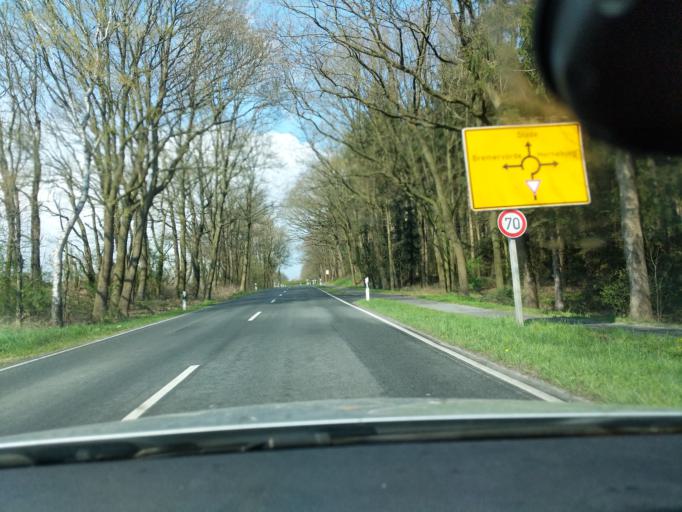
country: DE
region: Lower Saxony
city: Harsefeld
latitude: 53.4723
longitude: 9.4935
